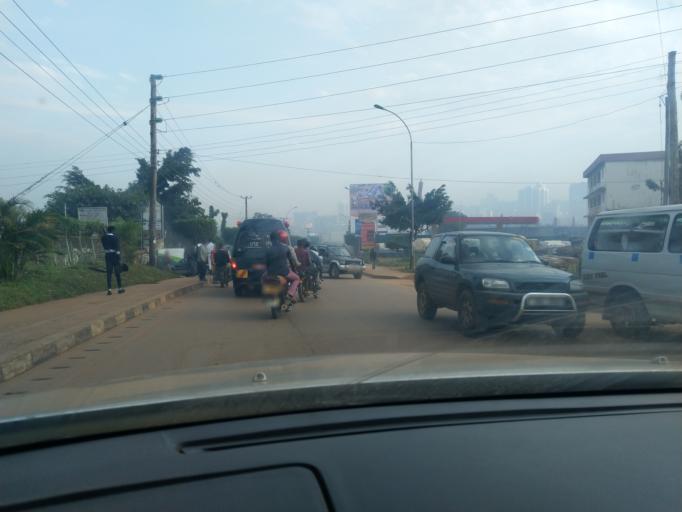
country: UG
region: Central Region
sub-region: Kampala District
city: Kampala
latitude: 0.3042
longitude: 32.5847
